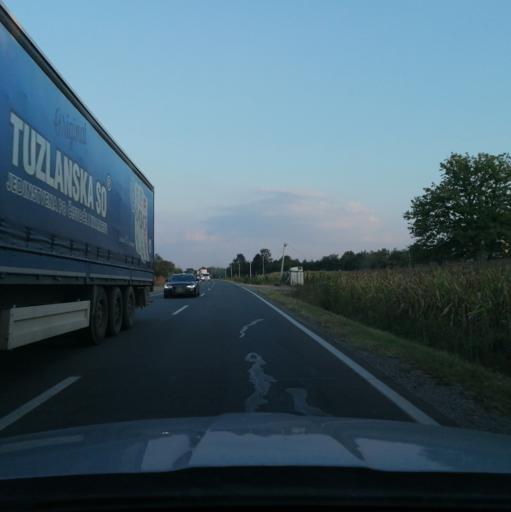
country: RS
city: Prislonica
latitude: 43.8452
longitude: 20.5657
